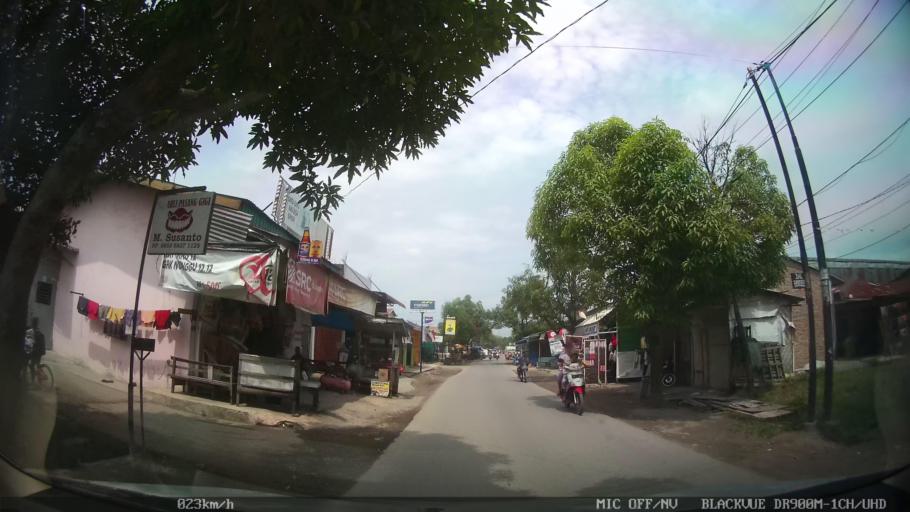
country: ID
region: North Sumatra
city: Medan
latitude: 3.6513
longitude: 98.6912
